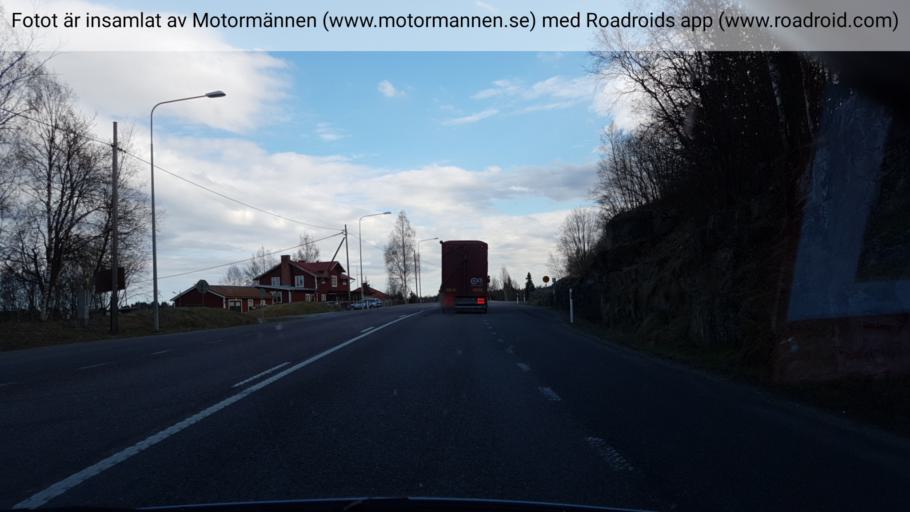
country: SE
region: Vaesternorrland
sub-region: Kramfors Kommun
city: Kramfors
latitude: 62.8905
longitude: 17.8521
